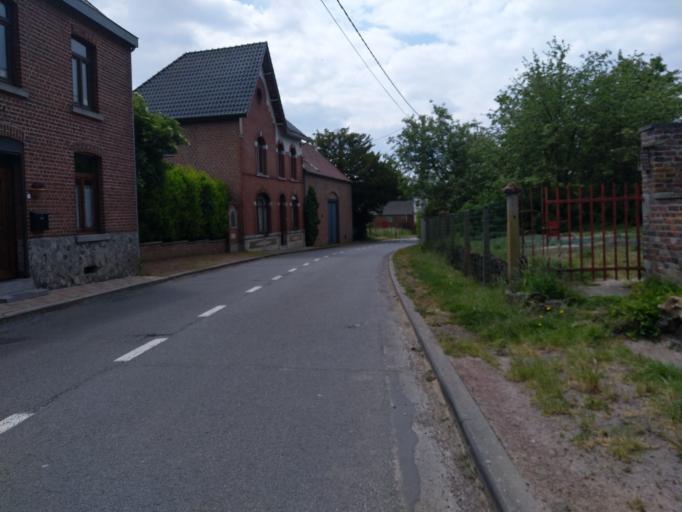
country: BE
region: Wallonia
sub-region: Province du Hainaut
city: Silly
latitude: 50.6024
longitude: 3.9412
